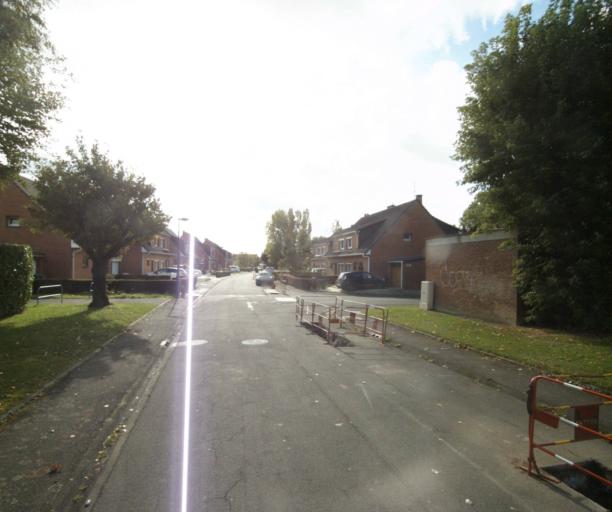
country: FR
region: Nord-Pas-de-Calais
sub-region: Departement du Nord
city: Armentieres
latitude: 50.6764
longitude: 2.8956
